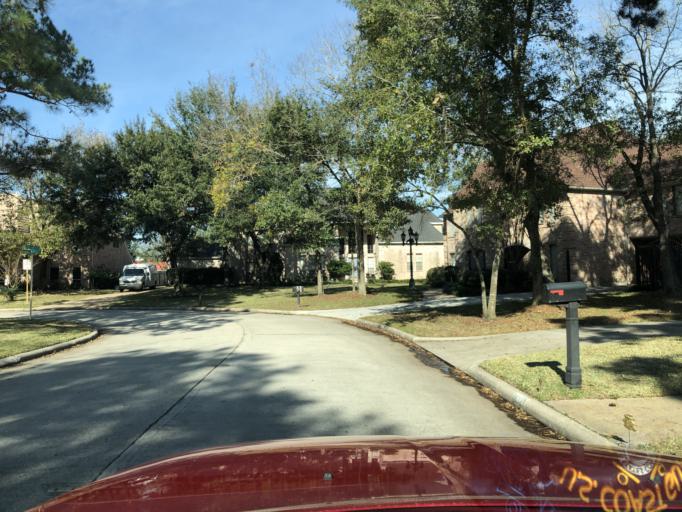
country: US
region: Texas
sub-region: Harris County
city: Tomball
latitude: 30.0311
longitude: -95.5520
